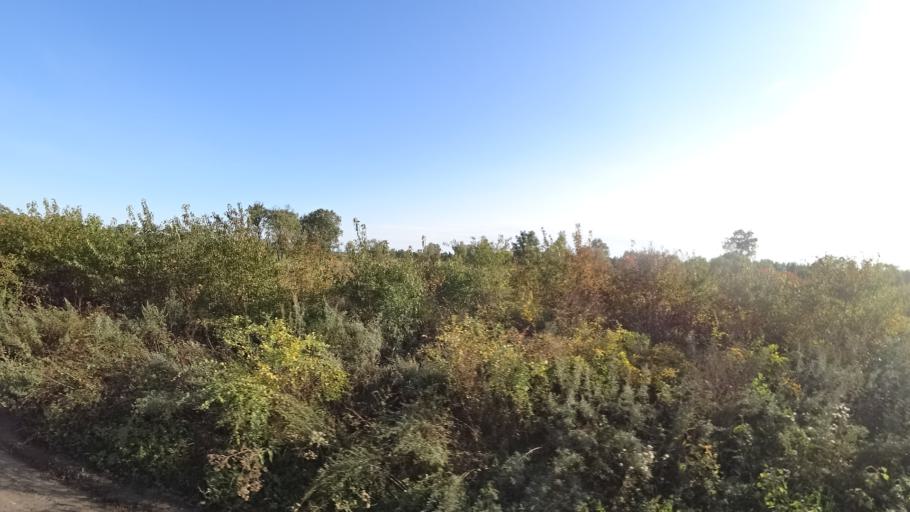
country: RU
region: Amur
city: Arkhara
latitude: 49.3557
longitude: 130.1311
